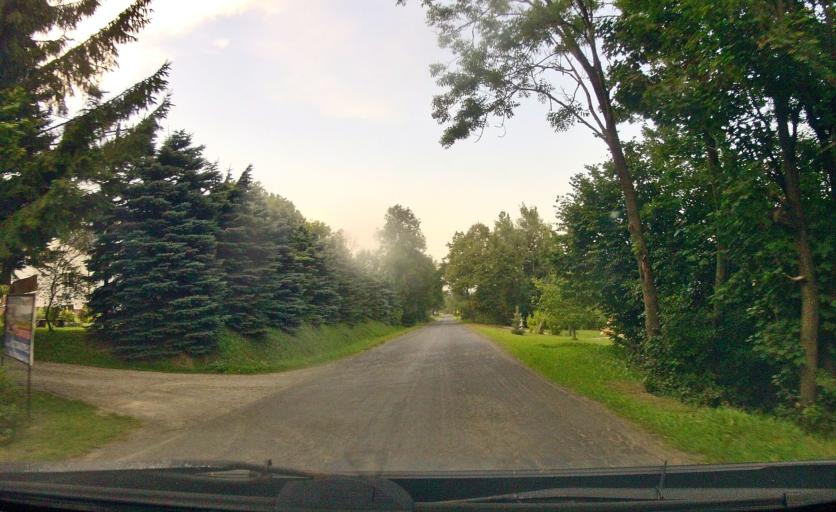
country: PL
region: Subcarpathian Voivodeship
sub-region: Powiat krosnienski
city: Dukla
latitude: 49.5376
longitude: 21.6159
